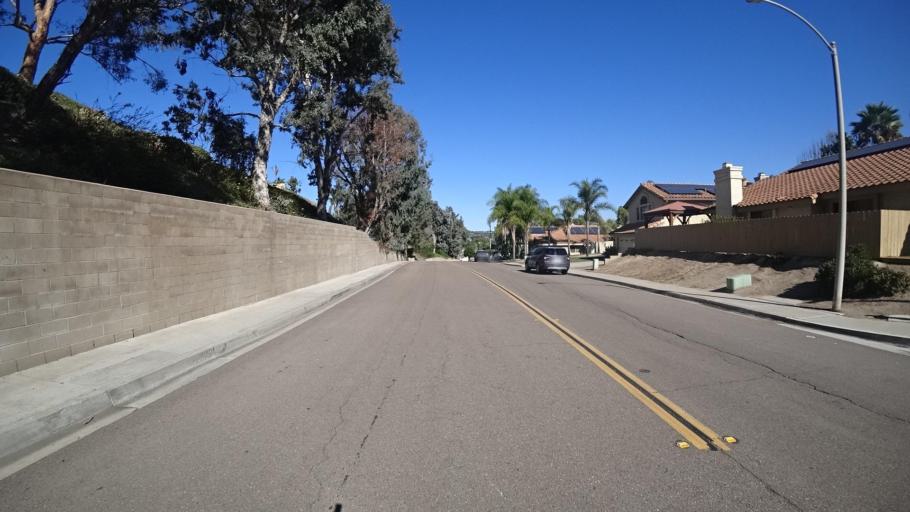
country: US
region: California
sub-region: San Diego County
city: Bonita
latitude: 32.6660
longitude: -117.0159
